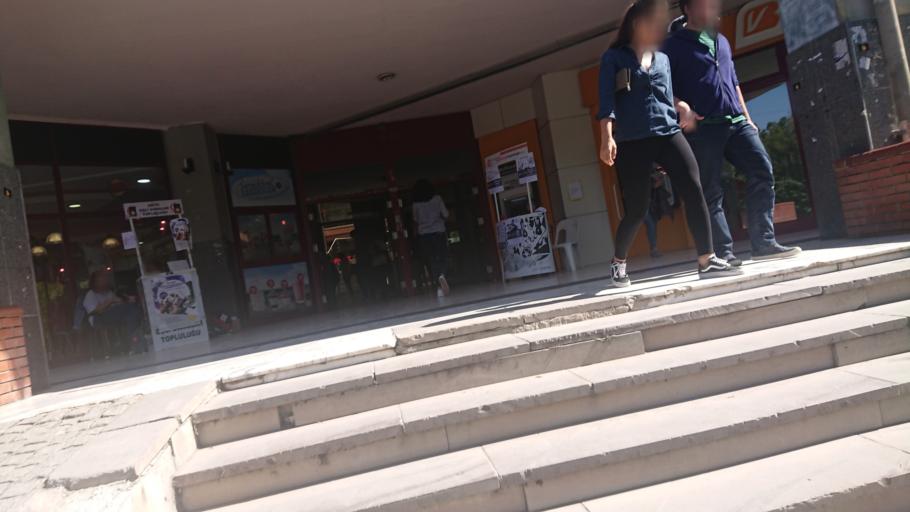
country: TR
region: Ankara
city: Ankara
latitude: 39.8925
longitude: 32.7879
